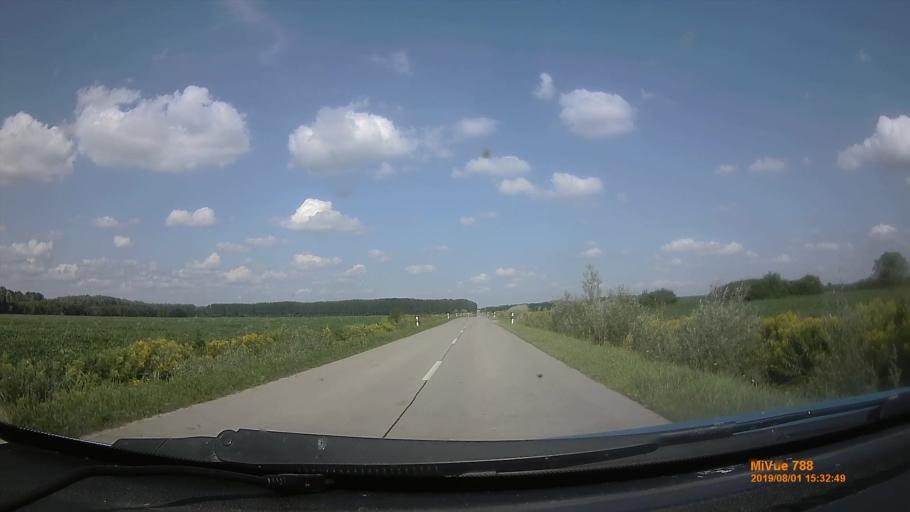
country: HU
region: Baranya
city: Sellye
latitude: 45.9515
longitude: 17.8698
